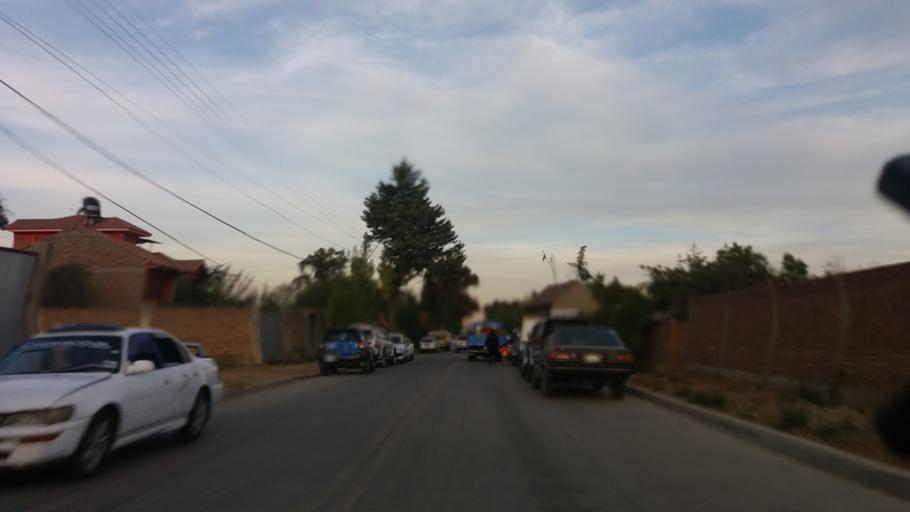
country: BO
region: Cochabamba
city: Cochabamba
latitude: -17.3671
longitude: -66.2140
